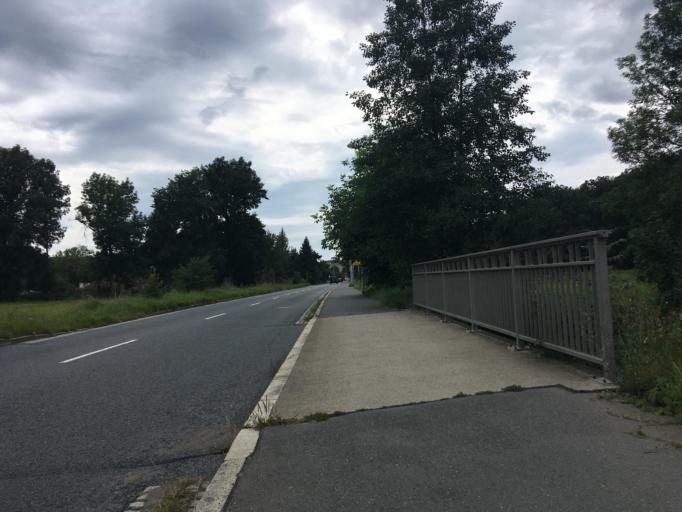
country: DE
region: Saxony
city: Dohma
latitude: 50.9363
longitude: 13.9199
